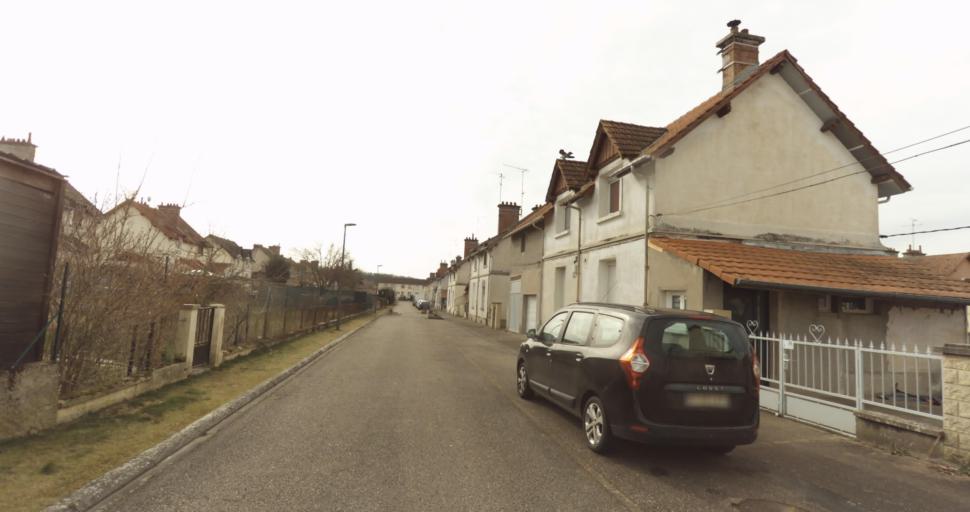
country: FR
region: Lorraine
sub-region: Departement de Meurthe-et-Moselle
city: Jarny
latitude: 49.1442
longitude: 5.8804
